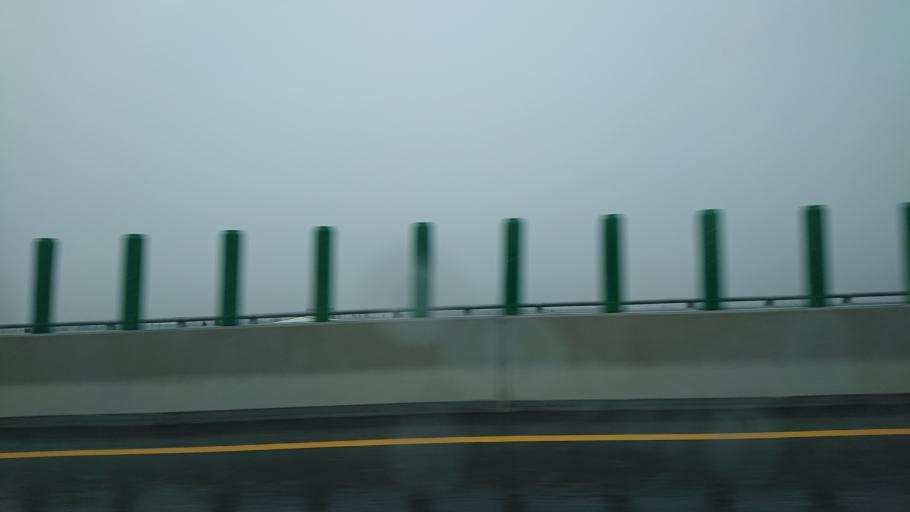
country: TW
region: Taiwan
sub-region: Changhua
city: Chang-hua
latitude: 23.9163
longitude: 120.3103
